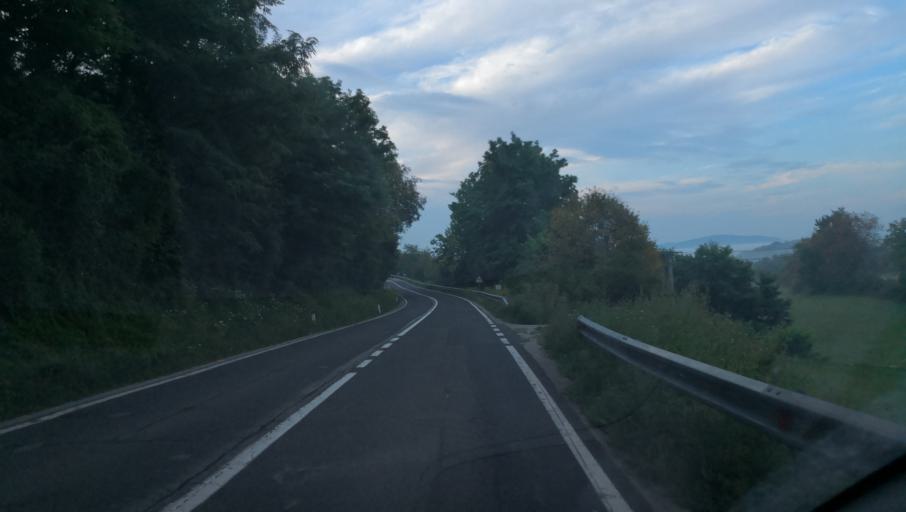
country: SI
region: Metlika
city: Metlika
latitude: 45.6562
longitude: 15.2952
